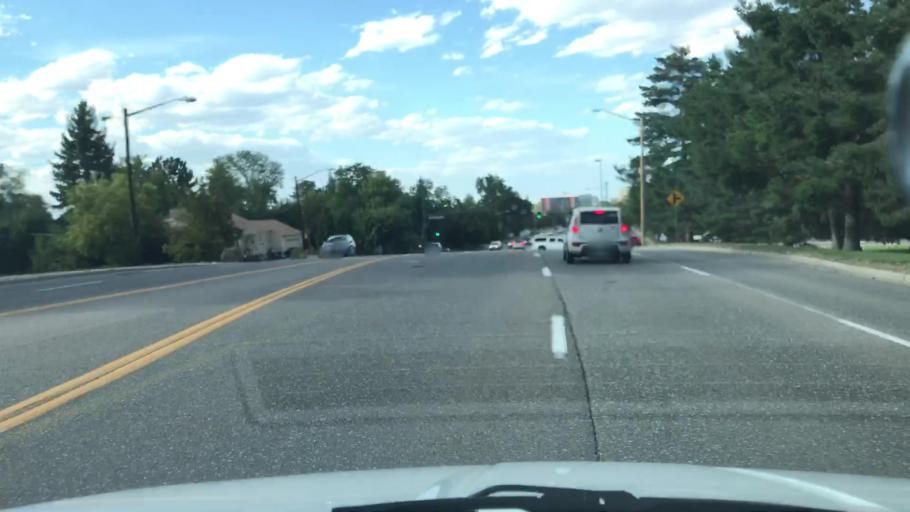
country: US
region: Colorado
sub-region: Arapahoe County
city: Cherry Hills Village
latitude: 39.6595
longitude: -104.9405
